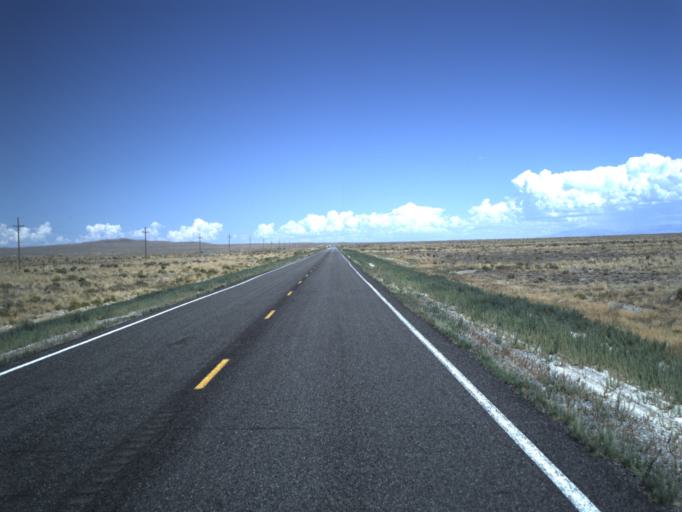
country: US
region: Utah
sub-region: Millard County
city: Delta
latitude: 39.1086
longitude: -113.1403
